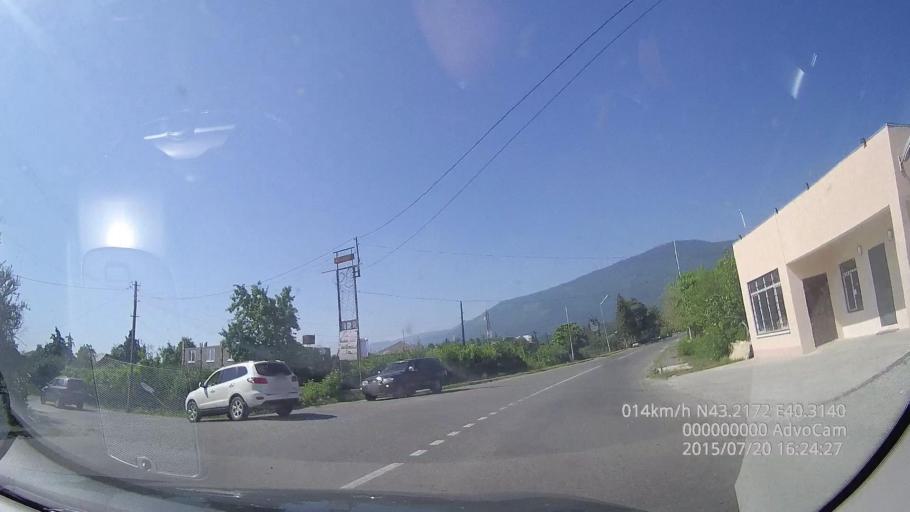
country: GE
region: Abkhazia
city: Bich'vinta
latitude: 43.2171
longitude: 40.3140
